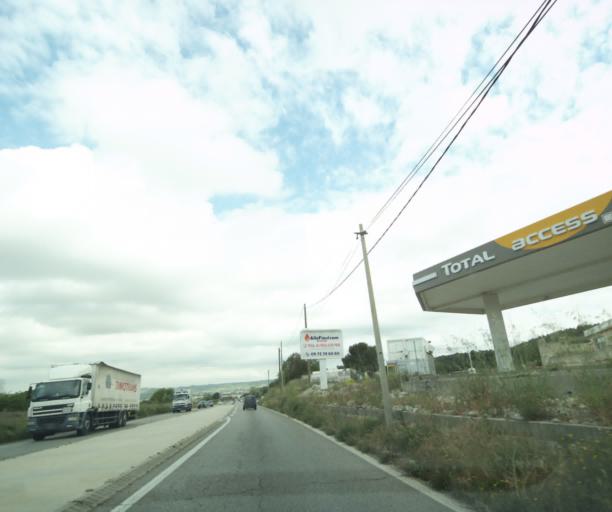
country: FR
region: Provence-Alpes-Cote d'Azur
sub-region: Departement des Bouches-du-Rhone
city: La Fare-les-Oliviers
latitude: 43.5186
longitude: 5.2003
